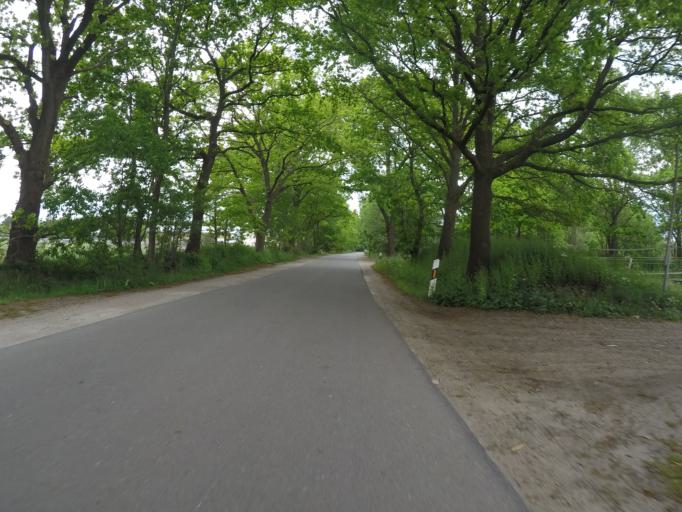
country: DE
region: Schleswig-Holstein
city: Norderstedt
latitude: 53.7071
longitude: 9.9708
